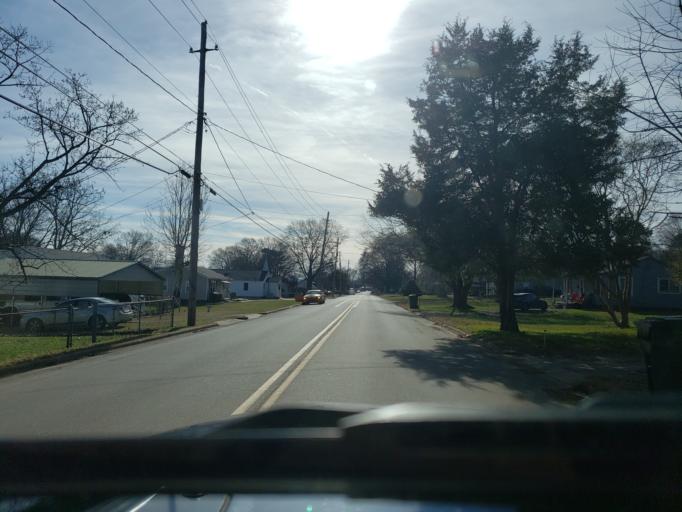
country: US
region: North Carolina
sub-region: Cleveland County
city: Kings Mountain
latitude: 35.2562
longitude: -81.3326
